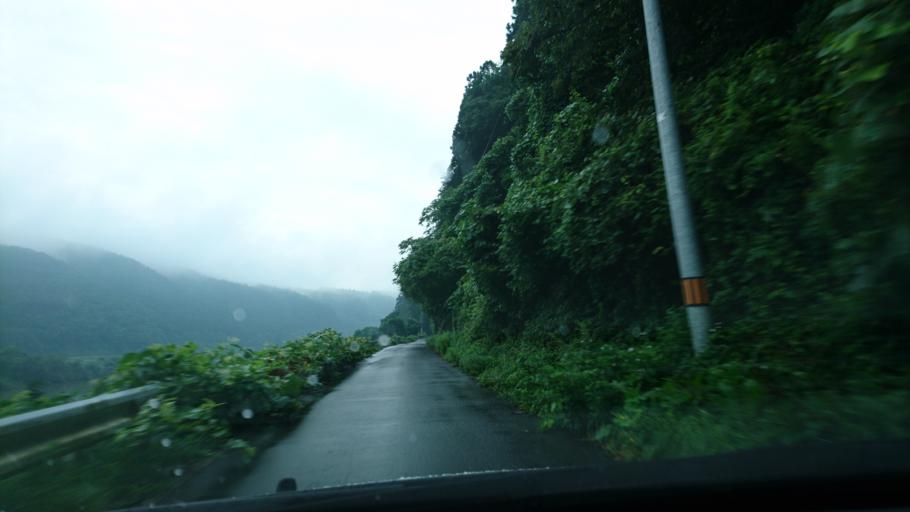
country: JP
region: Iwate
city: Ichinoseki
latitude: 38.8729
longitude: 141.2604
